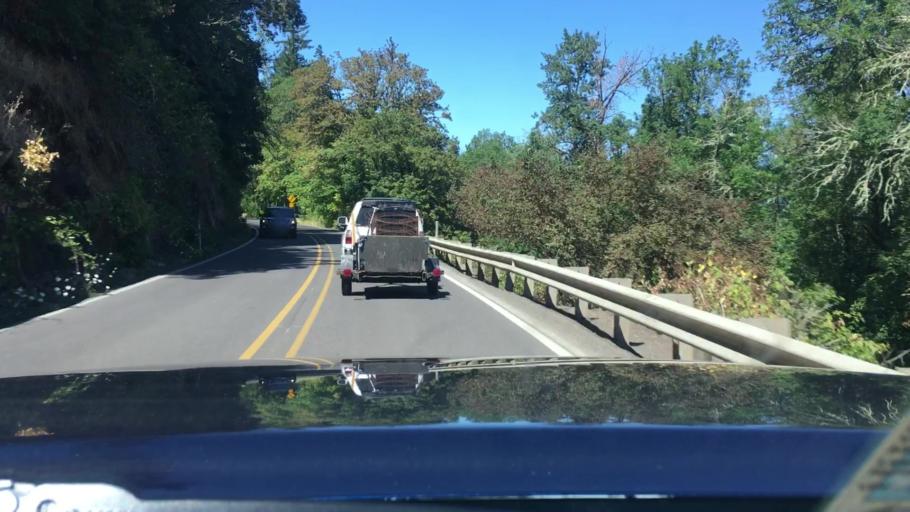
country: US
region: Oregon
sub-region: Lane County
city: Cottage Grove
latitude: 43.8229
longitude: -123.0459
